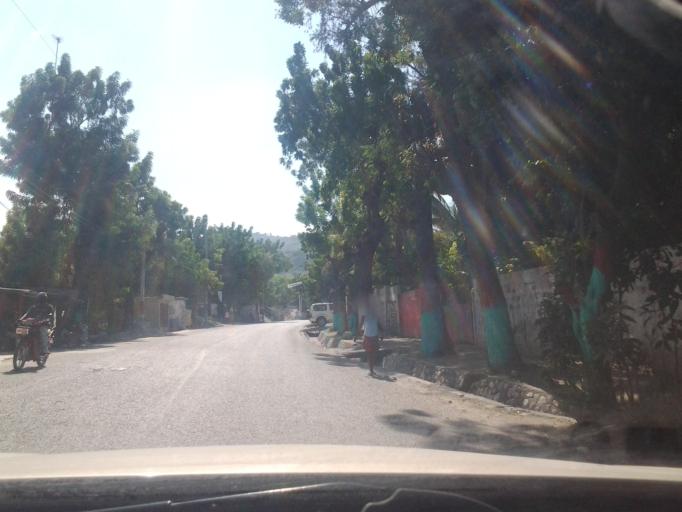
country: HT
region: Ouest
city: Leogane
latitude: 18.4500
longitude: -72.6353
